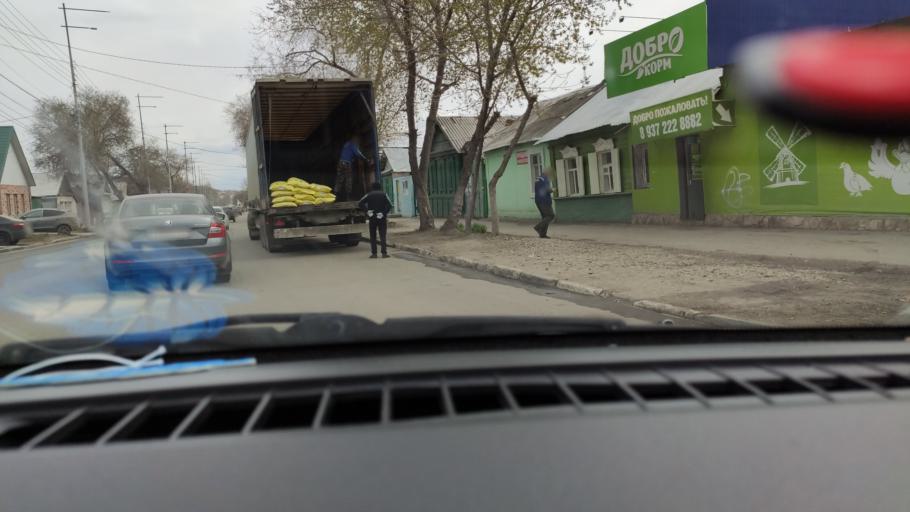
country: RU
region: Saratov
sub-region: Saratovskiy Rayon
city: Saratov
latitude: 51.5464
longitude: 46.0236
